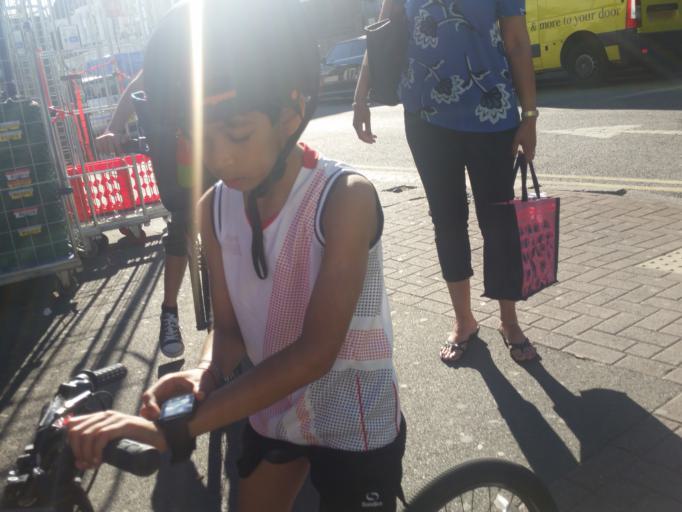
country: GB
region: England
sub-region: Greater London
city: Hammersmith
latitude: 51.5337
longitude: -0.2191
